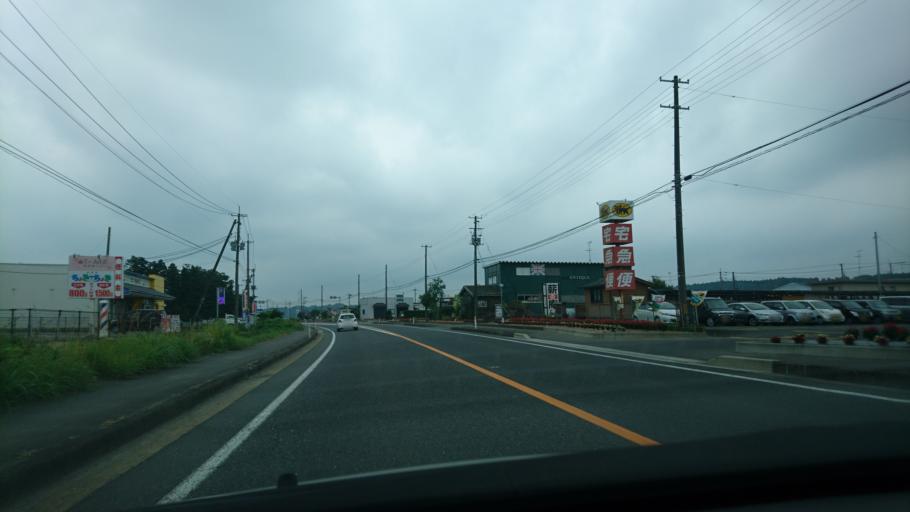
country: JP
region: Miyagi
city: Furukawa
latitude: 38.6476
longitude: 140.8774
